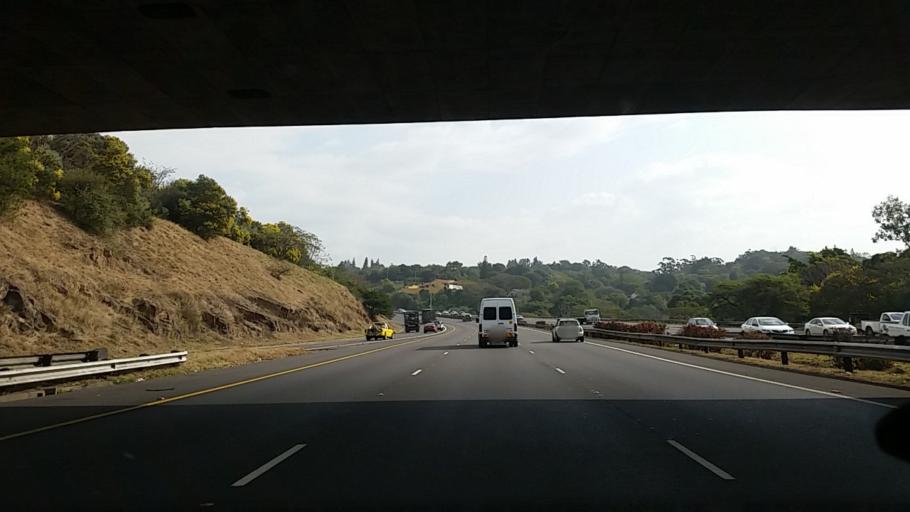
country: ZA
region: KwaZulu-Natal
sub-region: eThekwini Metropolitan Municipality
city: Berea
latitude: -29.8405
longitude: 30.9517
